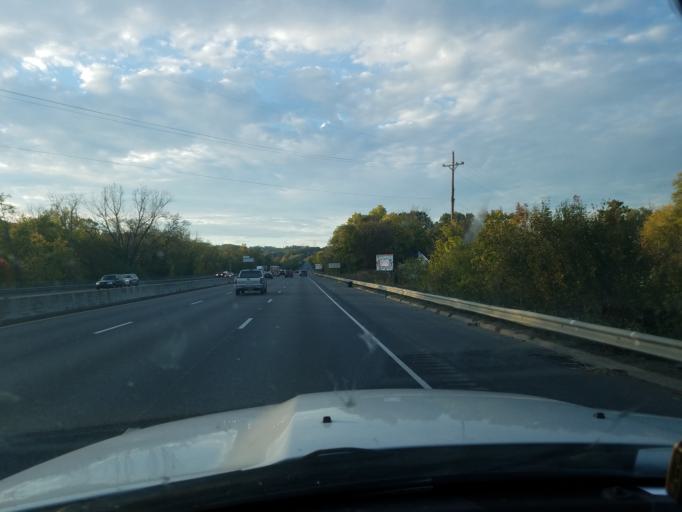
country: US
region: Indiana
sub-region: Floyd County
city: New Albany
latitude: 38.2916
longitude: -85.8360
